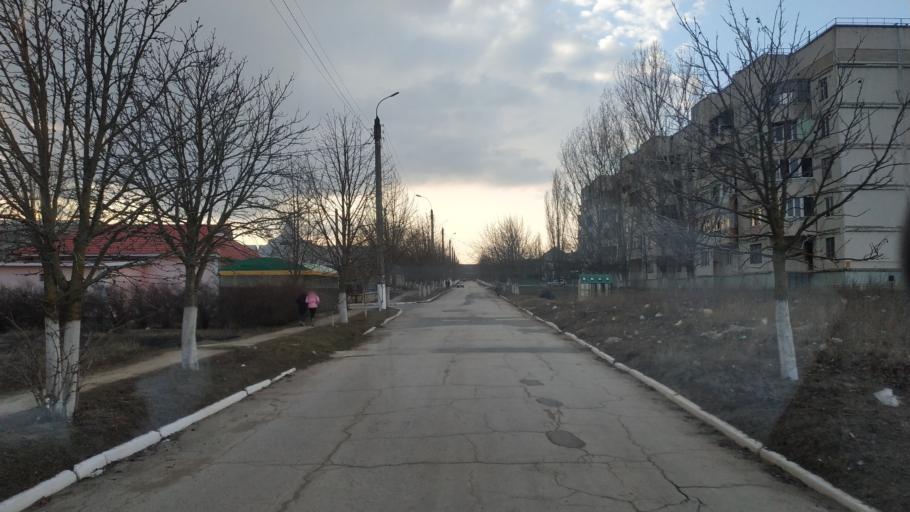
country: MD
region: Telenesti
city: Grigoriopol
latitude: 47.0123
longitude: 29.2935
